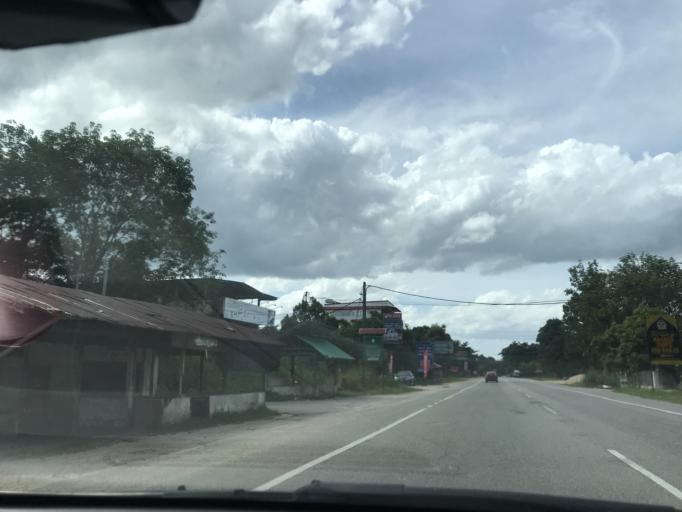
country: MY
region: Kelantan
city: Kampong Pangkal Kalong
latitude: 5.9124
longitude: 102.1877
